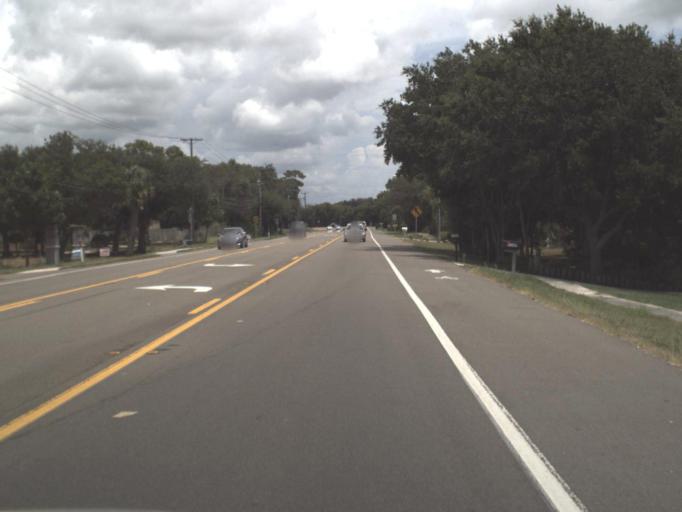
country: US
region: Florida
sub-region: Pinellas County
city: Dunedin
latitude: 28.0488
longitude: -82.7764
